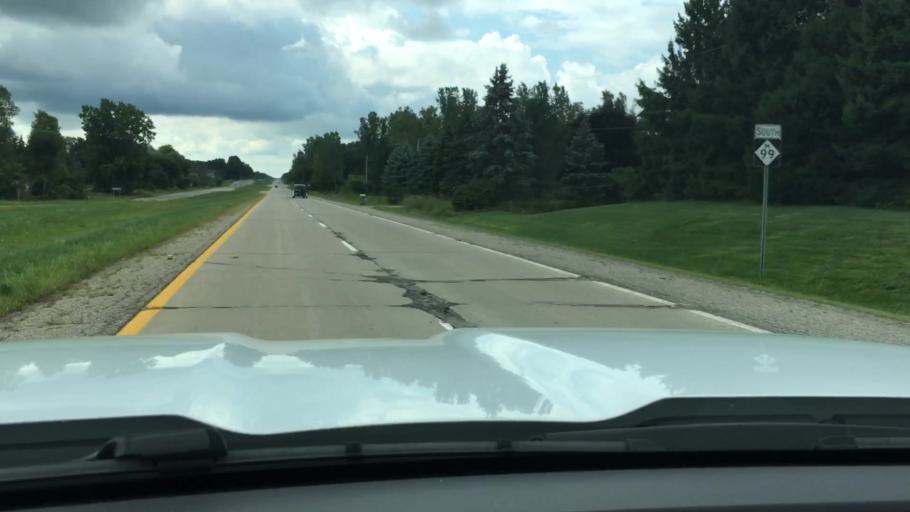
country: US
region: Michigan
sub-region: Eaton County
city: Dimondale
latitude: 42.6039
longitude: -84.6225
